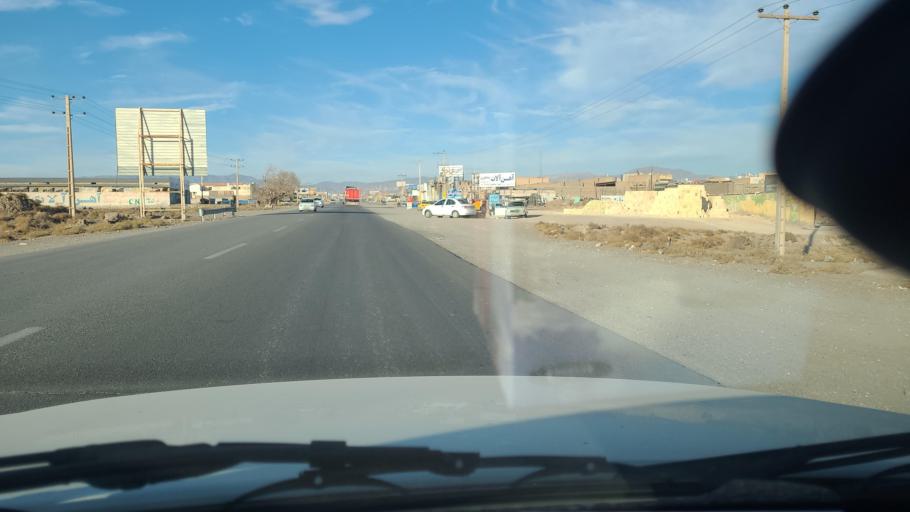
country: IR
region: Razavi Khorasan
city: Sabzevar
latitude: 36.2120
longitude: 57.6506
